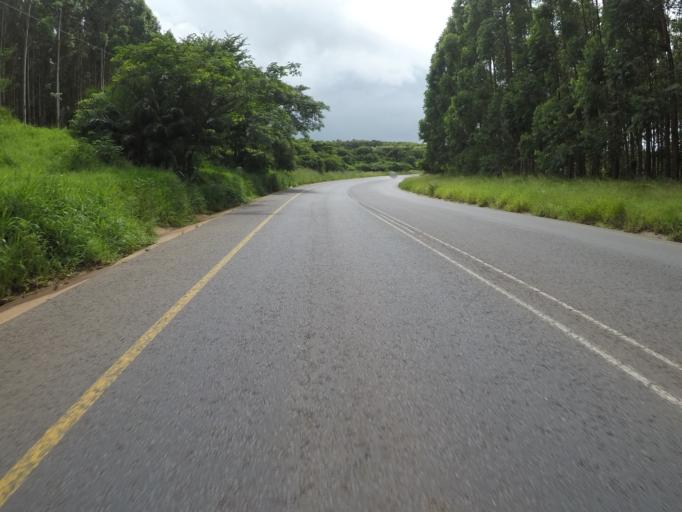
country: ZA
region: KwaZulu-Natal
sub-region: uThungulu District Municipality
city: eSikhawini
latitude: -28.8645
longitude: 31.8916
